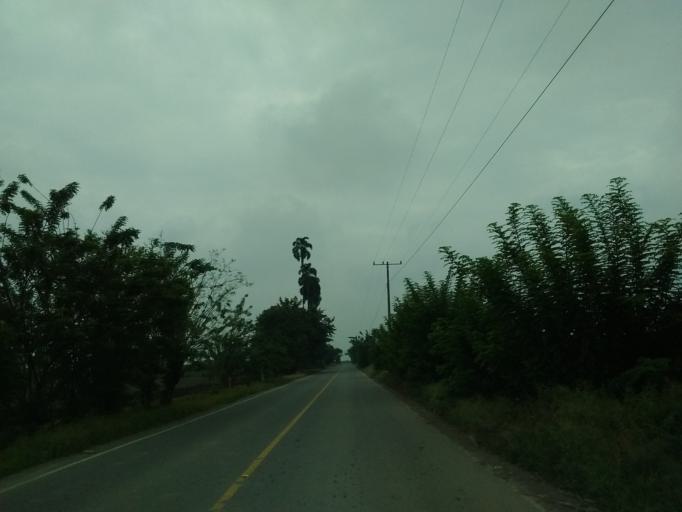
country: CO
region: Cauca
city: Puerto Tejada
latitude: 3.2229
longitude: -76.3690
